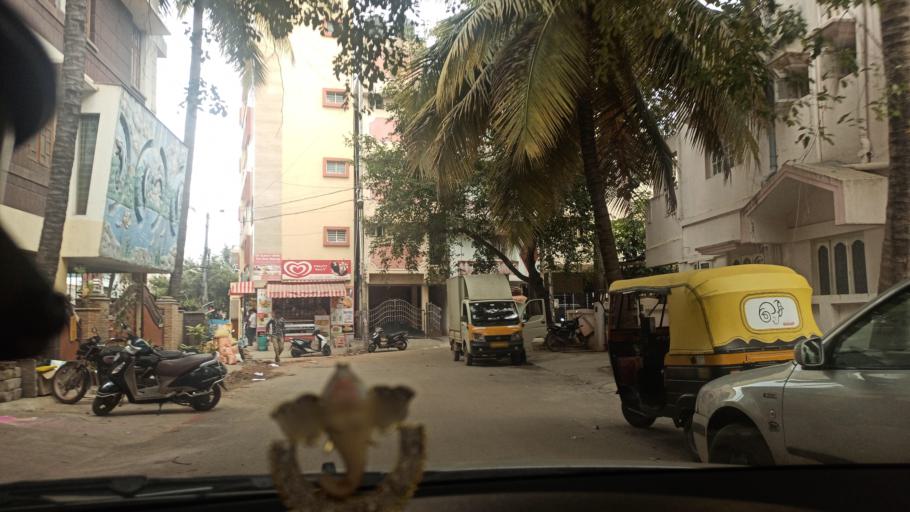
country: IN
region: Karnataka
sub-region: Bangalore Urban
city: Bangalore
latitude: 12.9206
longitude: 77.6474
